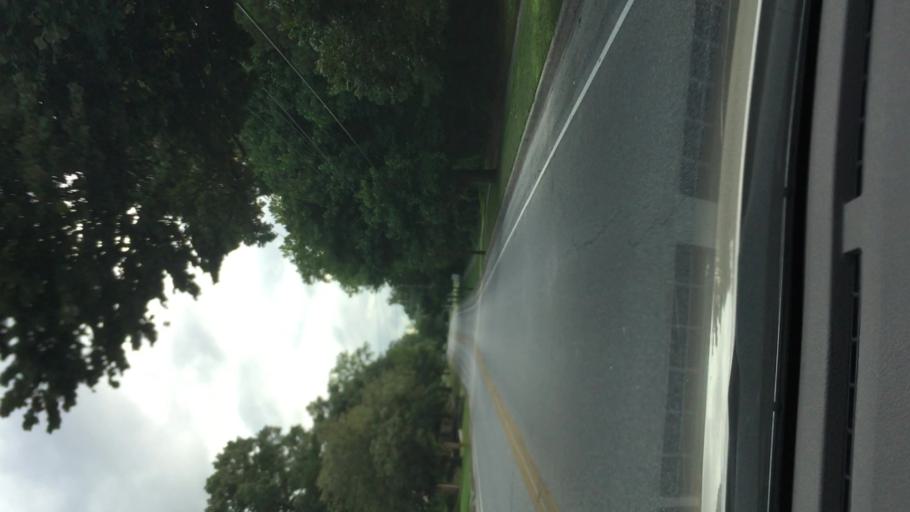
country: US
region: Maryland
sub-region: Wicomico County
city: Salisbury
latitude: 38.3579
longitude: -75.6101
